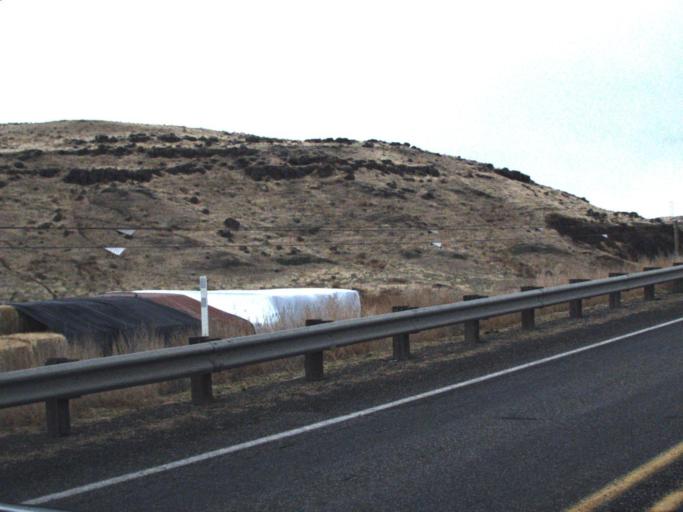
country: US
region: Washington
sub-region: Walla Walla County
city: Burbank
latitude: 46.0717
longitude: -118.7824
